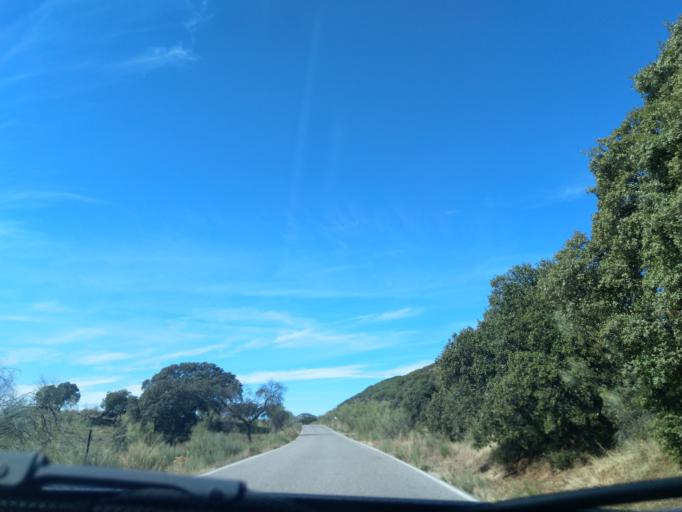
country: ES
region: Extremadura
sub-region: Provincia de Badajoz
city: Reina
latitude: 38.1166
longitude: -5.9267
